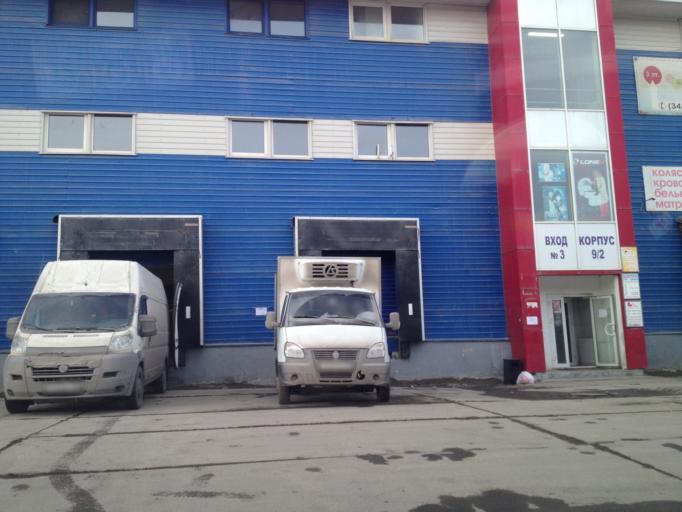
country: RU
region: Sverdlovsk
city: Istok
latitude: 56.7579
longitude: 60.7575
